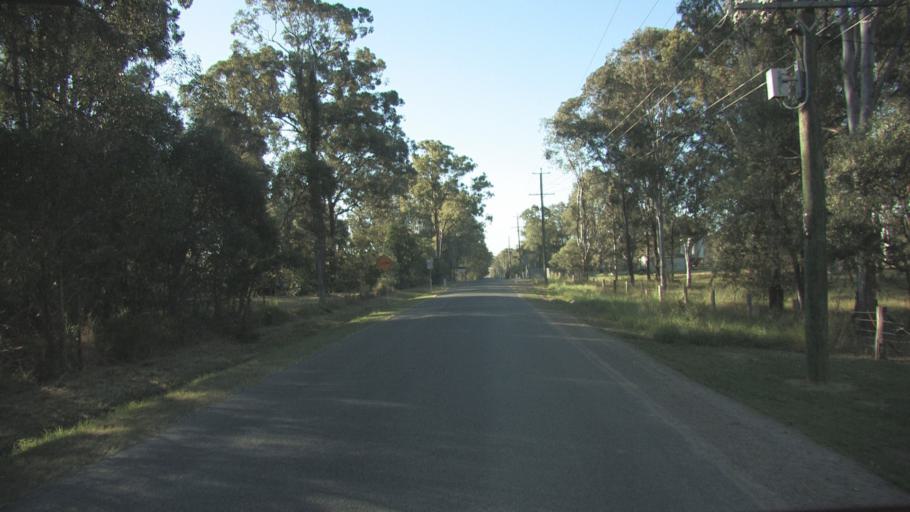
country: AU
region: Queensland
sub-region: Logan
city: Logan Reserve
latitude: -27.7623
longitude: 153.1391
